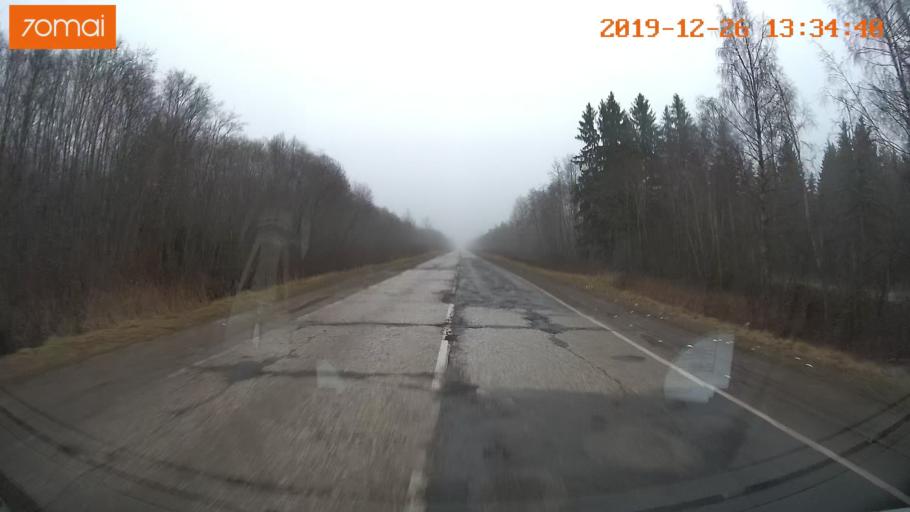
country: RU
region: Vologda
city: Sheksna
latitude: 58.8027
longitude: 38.3276
